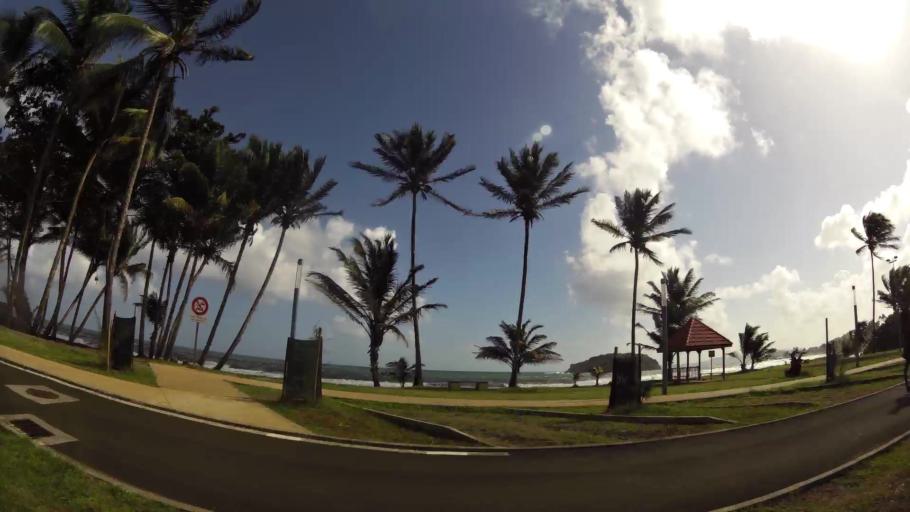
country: MQ
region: Martinique
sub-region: Martinique
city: Sainte-Marie
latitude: 14.7881
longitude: -60.9980
